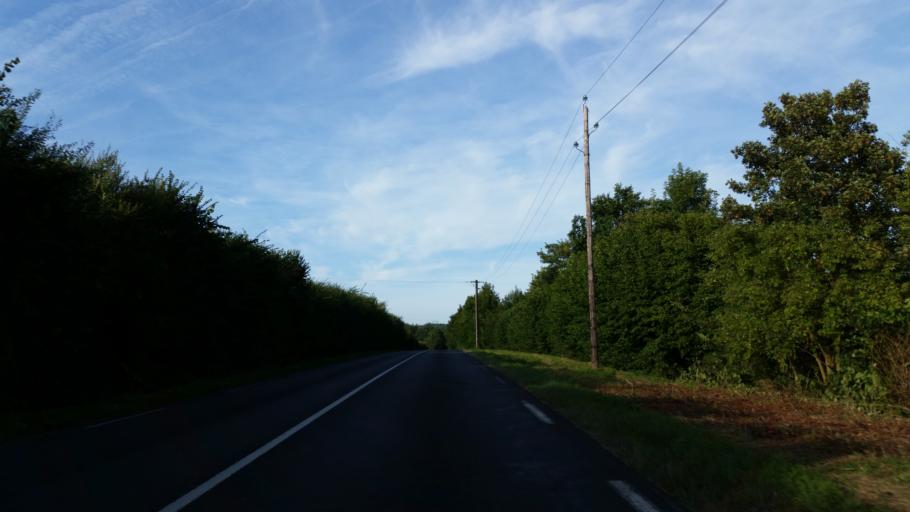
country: FR
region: Lower Normandy
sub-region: Departement du Calvados
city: Cambremer
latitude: 49.1877
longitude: 0.0479
